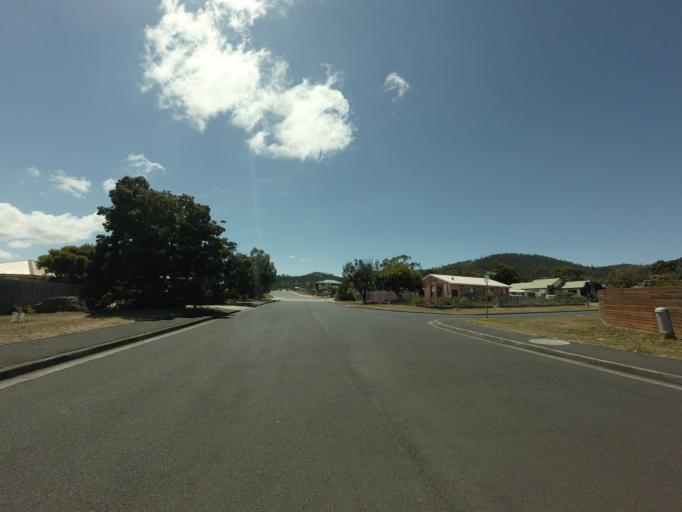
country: AU
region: Tasmania
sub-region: Clarence
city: Rokeby
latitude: -42.9013
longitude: 147.4515
